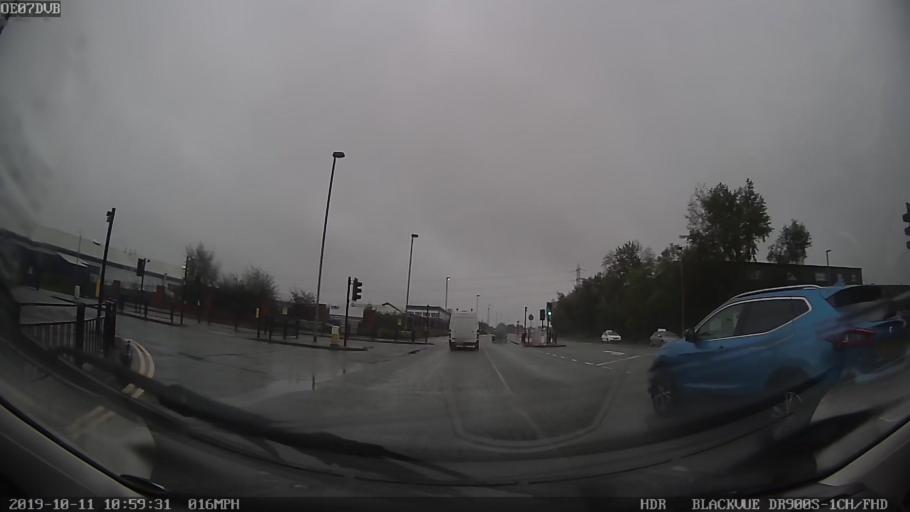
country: GB
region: England
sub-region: Manchester
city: Failsworth
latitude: 53.5322
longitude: -2.1747
